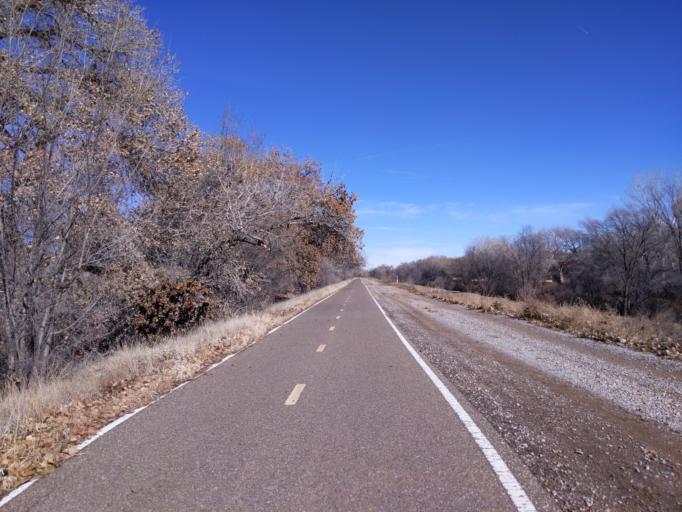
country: US
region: New Mexico
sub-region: Bernalillo County
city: Lee Acres
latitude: 35.1550
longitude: -106.6688
